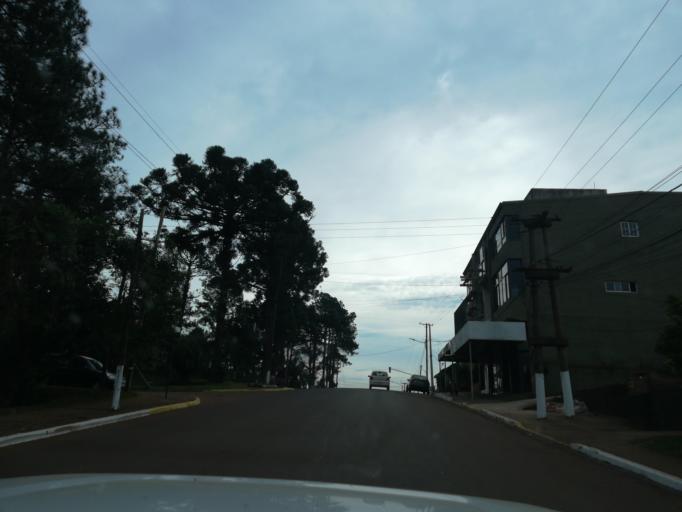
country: AR
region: Misiones
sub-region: Departamento de San Pedro
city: San Pedro
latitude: -26.6261
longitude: -54.1136
